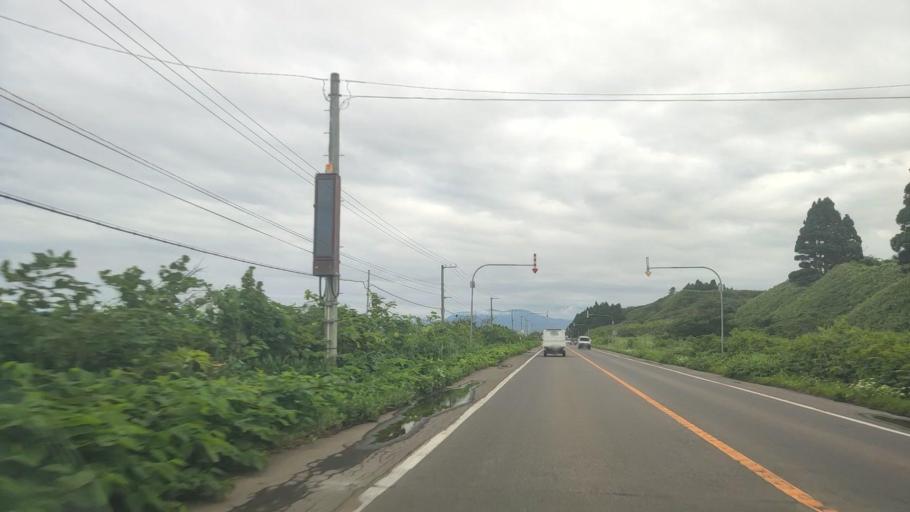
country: JP
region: Hokkaido
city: Niseko Town
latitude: 42.3467
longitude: 140.2825
